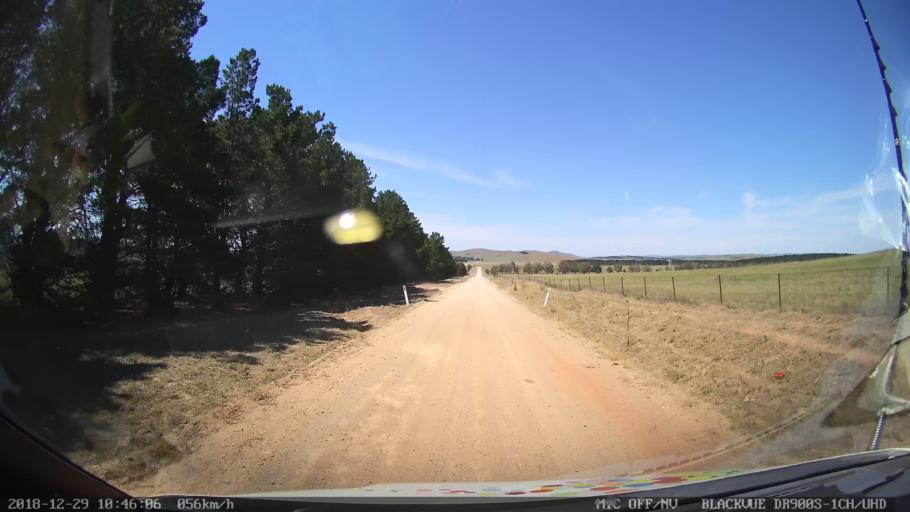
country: AU
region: New South Wales
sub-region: Palerang
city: Bungendore
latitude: -35.0473
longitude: 149.5168
